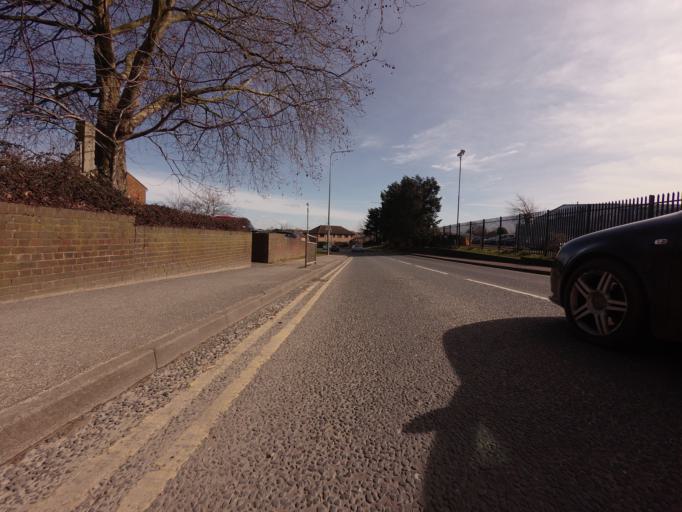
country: GB
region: England
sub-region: Kent
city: Swanley
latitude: 51.3944
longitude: 0.1764
